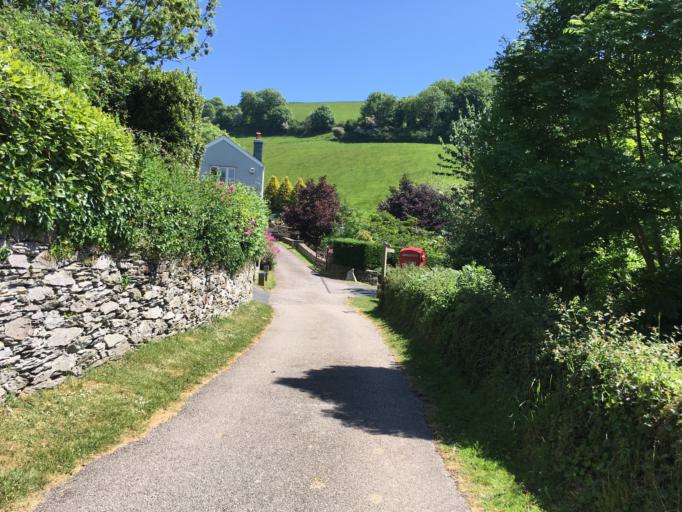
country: GB
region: England
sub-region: Devon
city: Dartmouth
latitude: 50.3461
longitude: -3.5528
